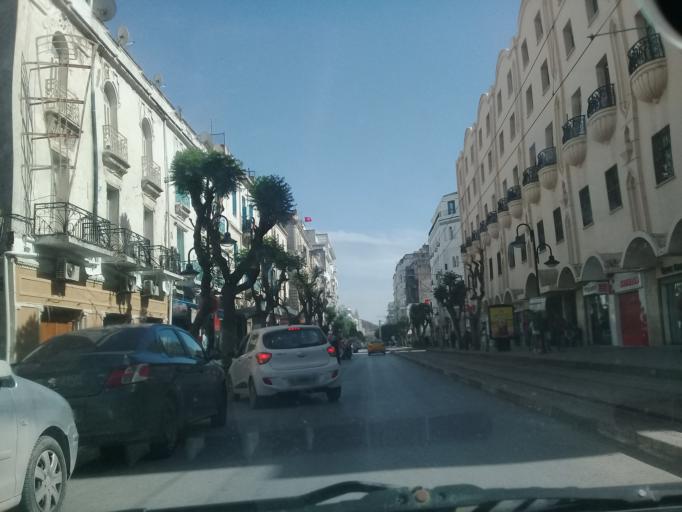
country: TN
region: Tunis
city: Tunis
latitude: 36.7992
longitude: 10.1814
